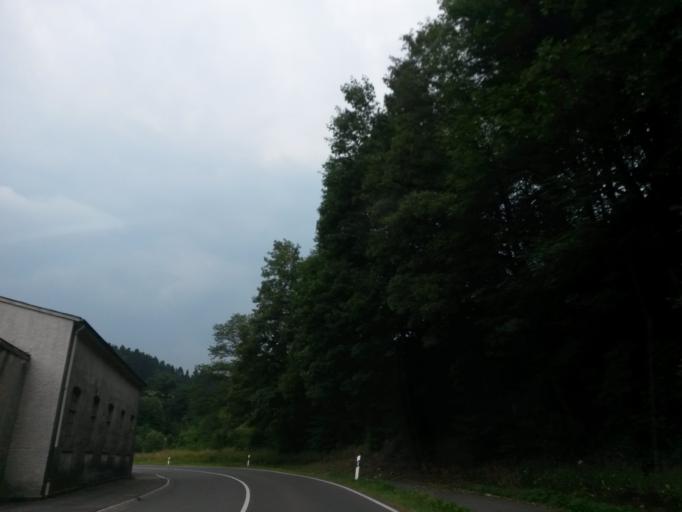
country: DE
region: North Rhine-Westphalia
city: Meinerzhagen
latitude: 51.0669
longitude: 7.6544
